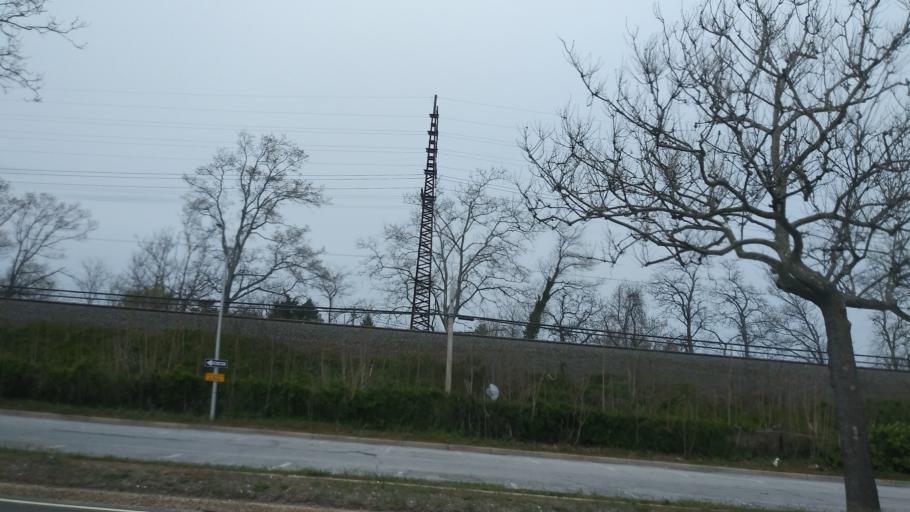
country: US
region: New York
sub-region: Nassau County
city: Baldwin
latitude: 40.6565
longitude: -73.6123
